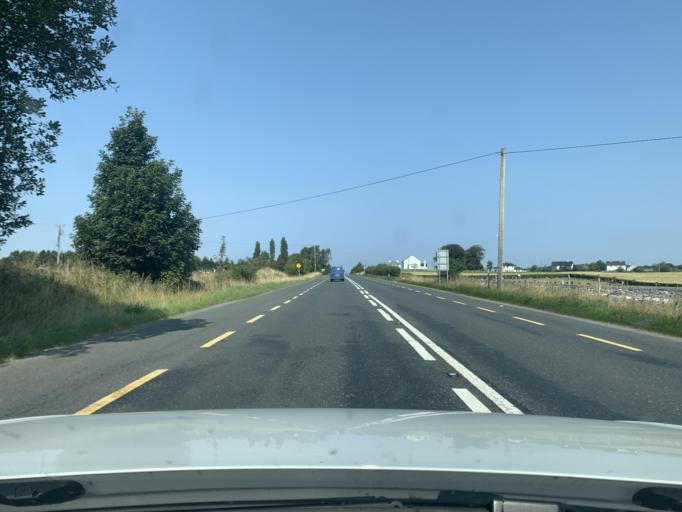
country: IE
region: Leinster
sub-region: An Iarmhi
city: Athlone
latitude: 53.5256
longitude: -8.0599
